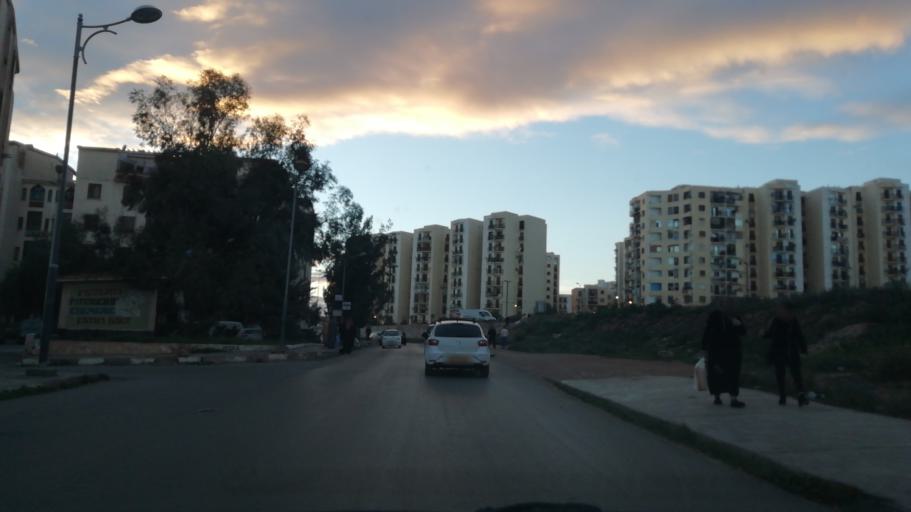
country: DZ
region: Oran
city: Bir el Djir
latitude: 35.6987
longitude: -0.5676
